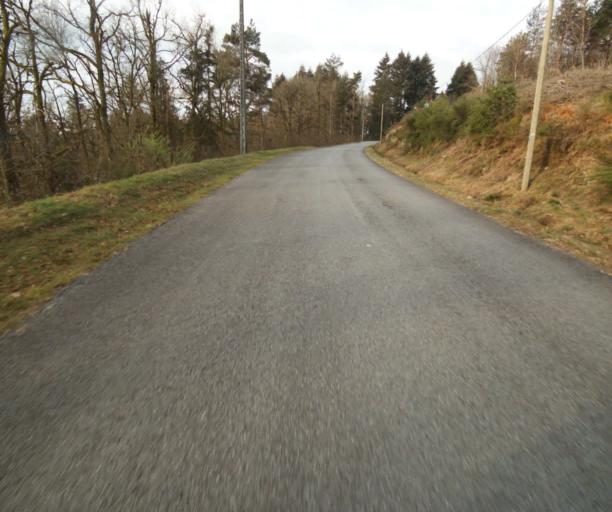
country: FR
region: Limousin
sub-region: Departement de la Correze
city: Correze
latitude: 45.4178
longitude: 1.8935
